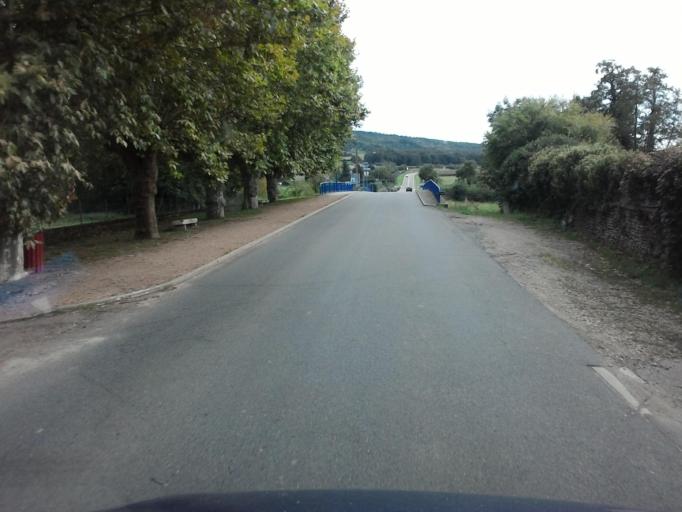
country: FR
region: Bourgogne
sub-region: Departement de Saone-et-Loire
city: Cluny
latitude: 46.5160
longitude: 4.5970
